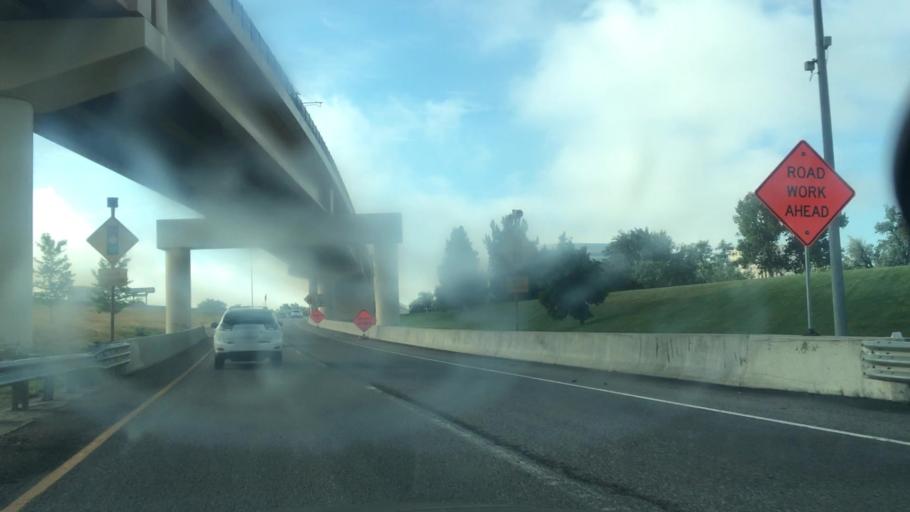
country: US
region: Colorado
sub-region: Arapahoe County
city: Castlewood
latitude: 39.6089
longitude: -104.8941
